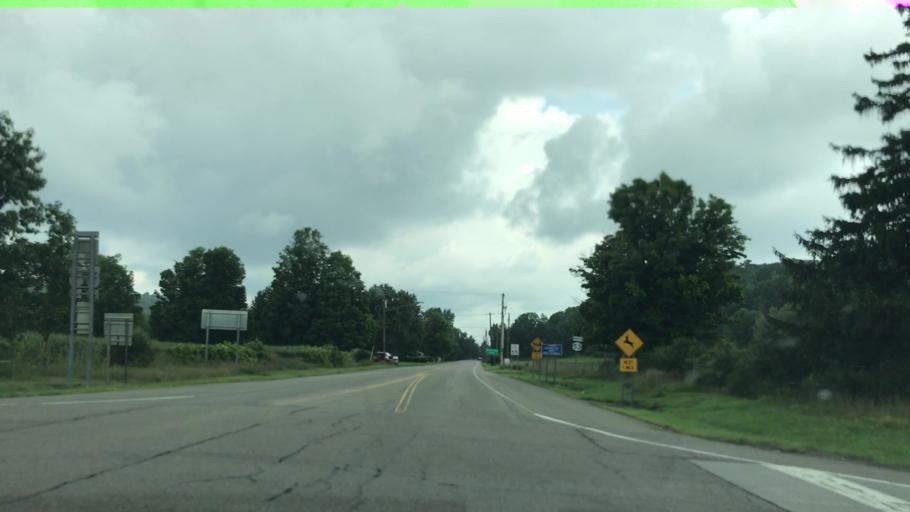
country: US
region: New York
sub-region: Steuben County
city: Bath
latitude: 42.3792
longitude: -77.3619
